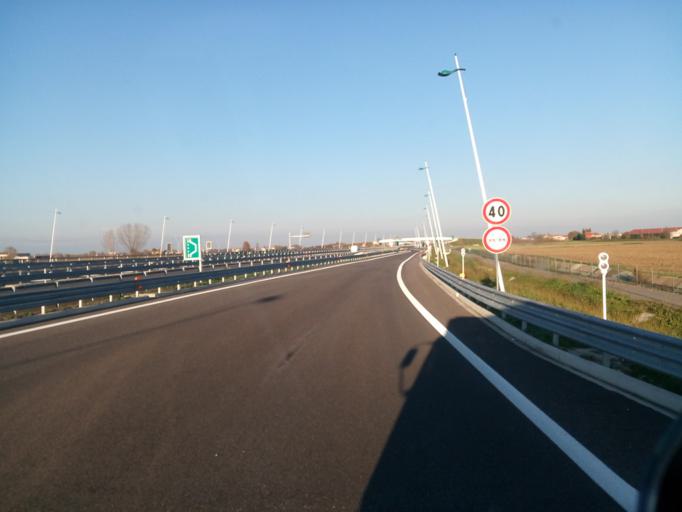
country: IT
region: Veneto
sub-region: Provincia di Padova
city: Bastia
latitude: 45.3898
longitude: 11.6166
